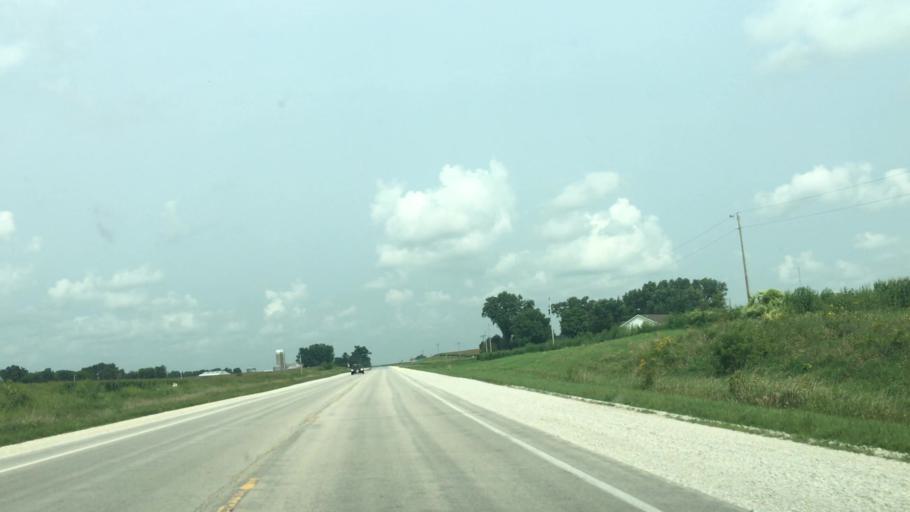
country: US
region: Iowa
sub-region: Winneshiek County
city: Decorah
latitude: 43.4074
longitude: -91.8548
